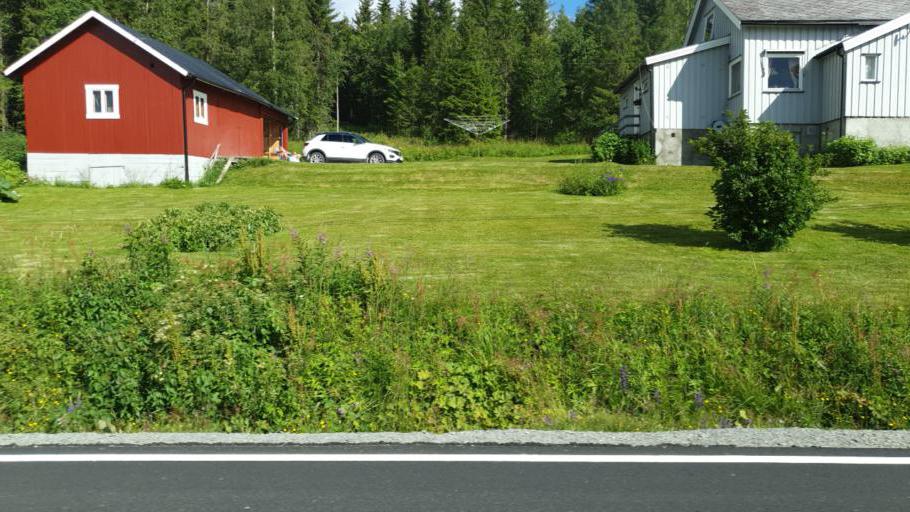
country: NO
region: Oppland
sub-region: Oystre Slidre
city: Heggenes
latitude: 61.1767
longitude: 8.9957
